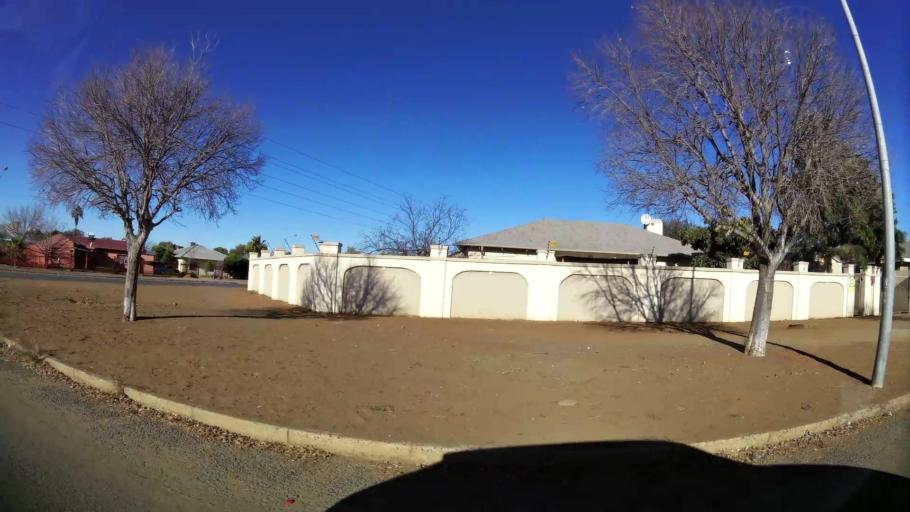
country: ZA
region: Northern Cape
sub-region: Frances Baard District Municipality
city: Kimberley
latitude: -28.7593
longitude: 24.7780
